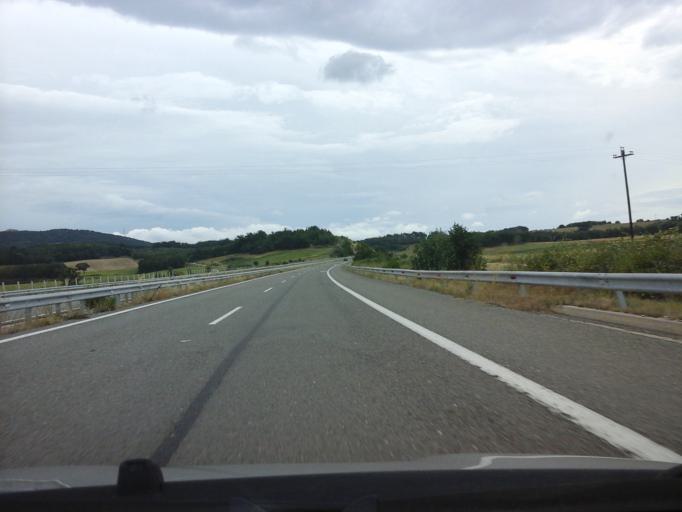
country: GR
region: East Macedonia and Thrace
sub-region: Nomos Evrou
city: Alexandroupoli
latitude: 40.9279
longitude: 25.9902
